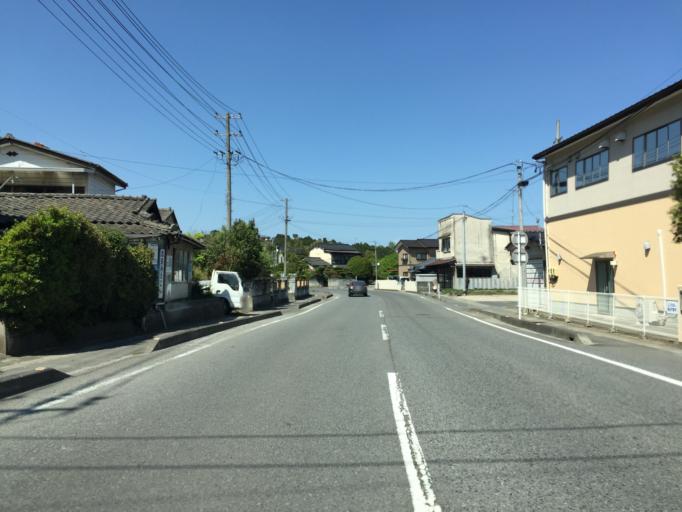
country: JP
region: Fukushima
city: Iwaki
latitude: 37.0353
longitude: 140.8527
